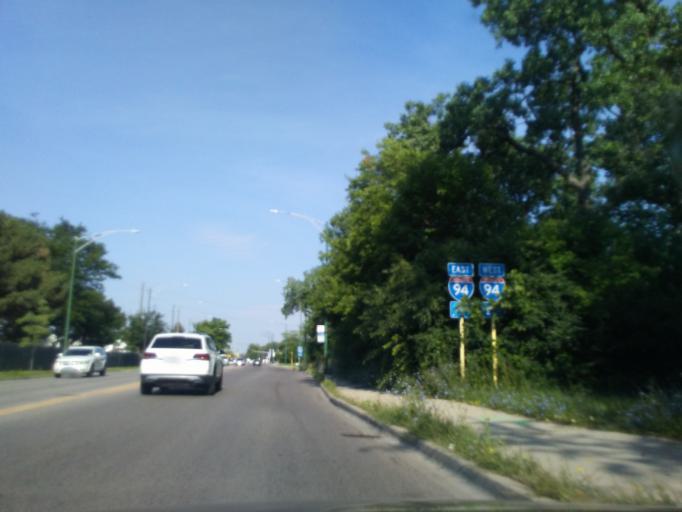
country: US
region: Illinois
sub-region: Cook County
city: Lincolnwood
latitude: 41.9755
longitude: -87.7442
